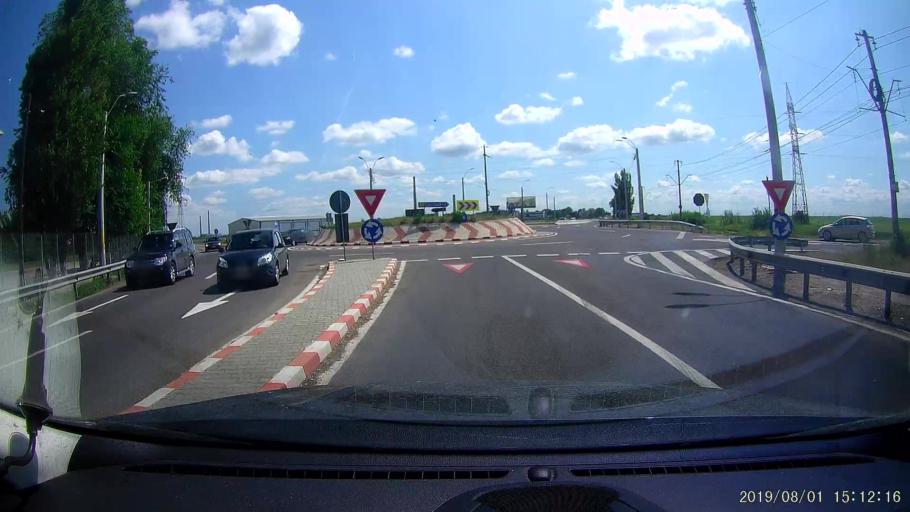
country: RO
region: Braila
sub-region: Comuna Chiscani
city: Lacu Sarat
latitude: 45.2077
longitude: 27.9151
